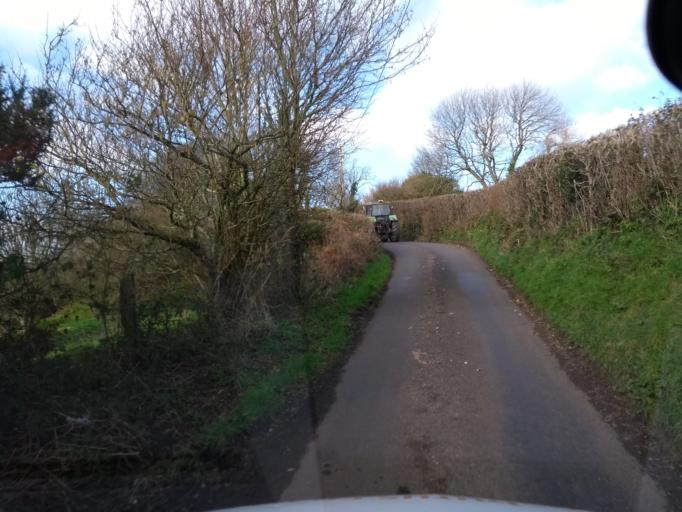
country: GB
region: England
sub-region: Somerset
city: Chard
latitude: 50.9326
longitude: -3.0206
